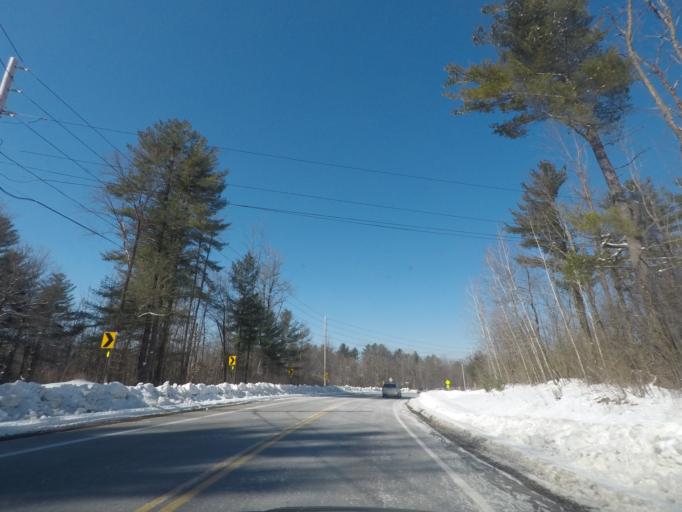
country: US
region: New York
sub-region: Saratoga County
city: Ballston Spa
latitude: 42.9986
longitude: -73.8252
